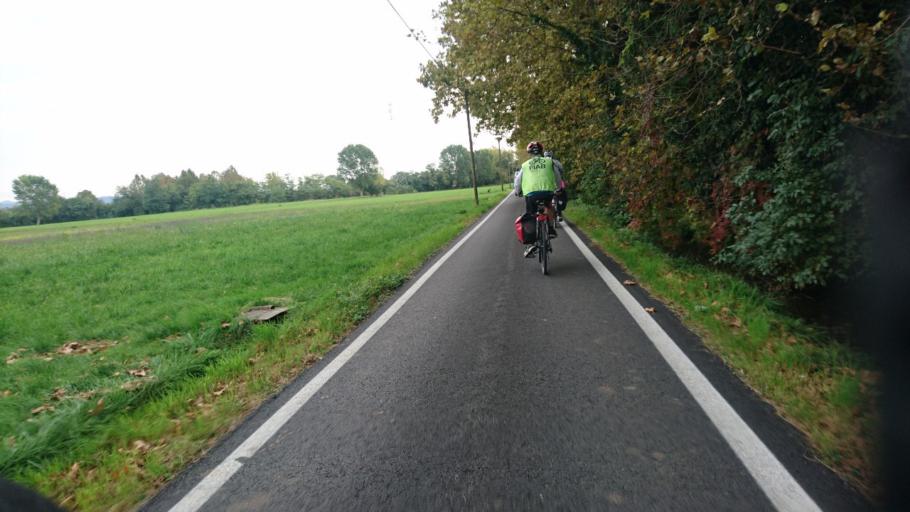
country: IT
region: Veneto
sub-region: Provincia di Verona
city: San Martino Buon Albergo
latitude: 45.4105
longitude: 11.1028
